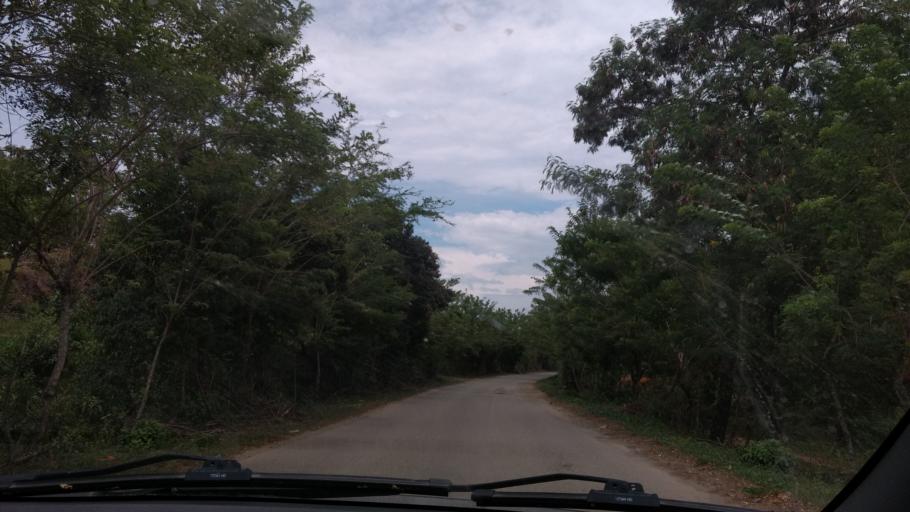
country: CO
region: Cauca
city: Buenos Aires
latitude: 3.0792
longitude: -76.6486
